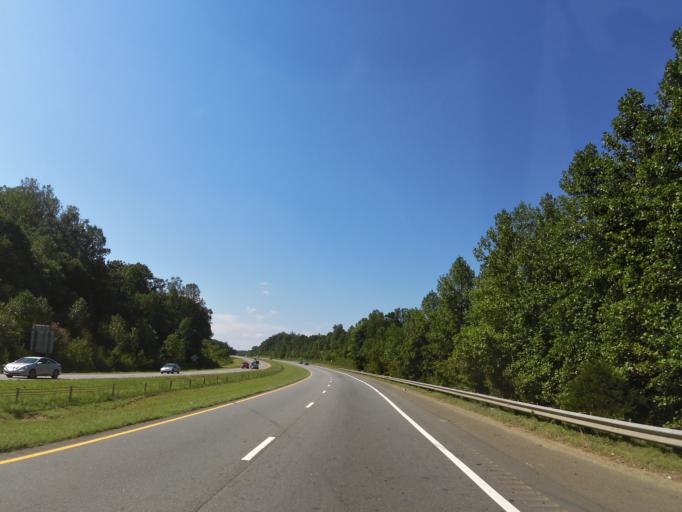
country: US
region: North Carolina
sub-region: Catawba County
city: Mountain View
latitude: 35.6443
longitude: -81.3042
